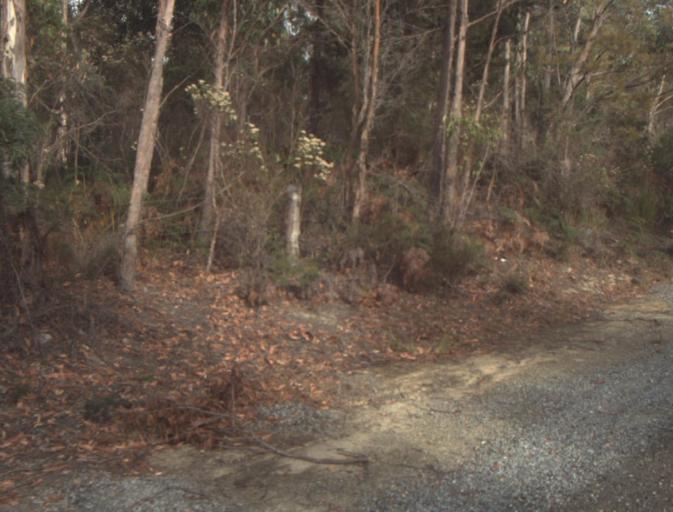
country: AU
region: Tasmania
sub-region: Dorset
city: Bridport
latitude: -41.1389
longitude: 147.2273
